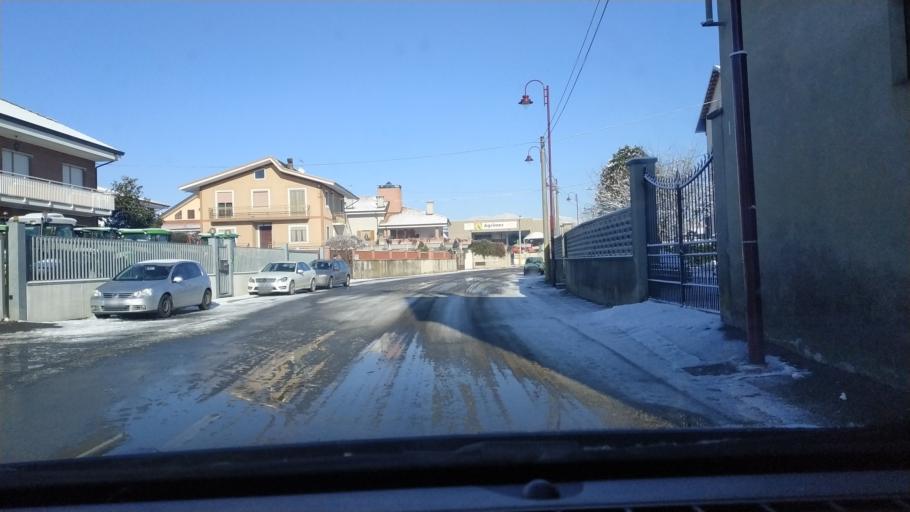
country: IT
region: Piedmont
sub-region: Provincia di Torino
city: Vische
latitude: 45.3350
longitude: 7.9499
